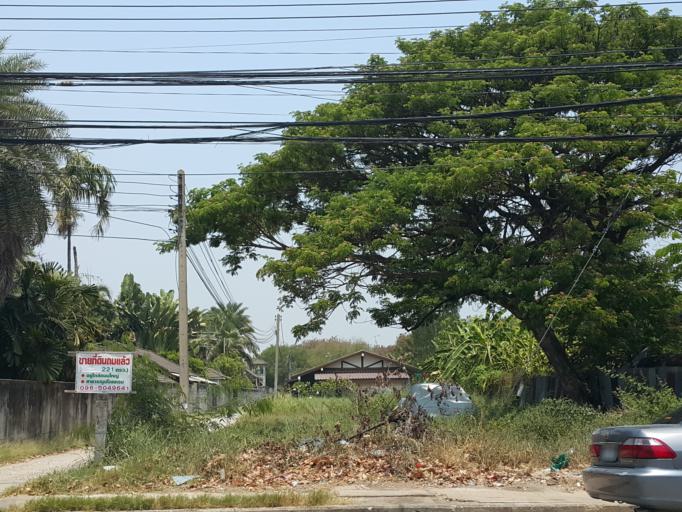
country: TH
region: Phitsanulok
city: Phitsanulok
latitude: 16.8111
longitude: 100.2542
